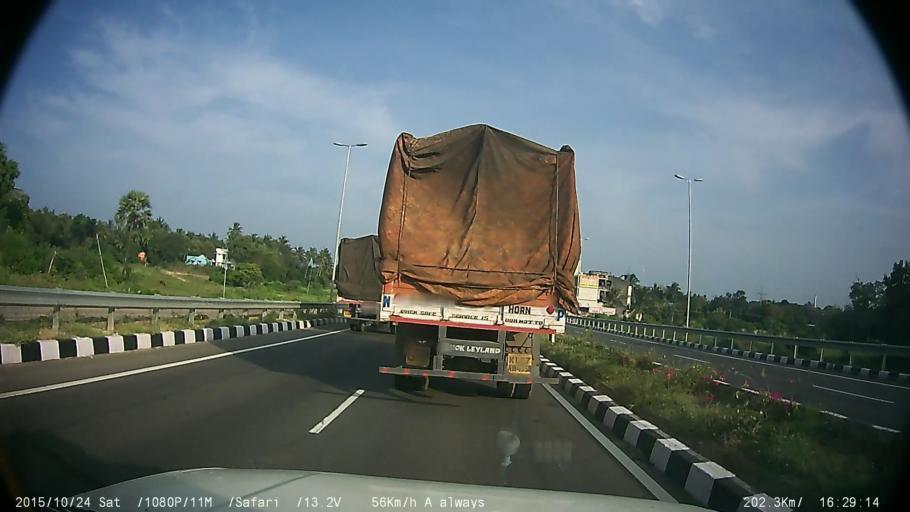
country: IN
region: Kerala
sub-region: Palakkad district
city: Chittur
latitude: 10.7981
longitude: 76.7618
